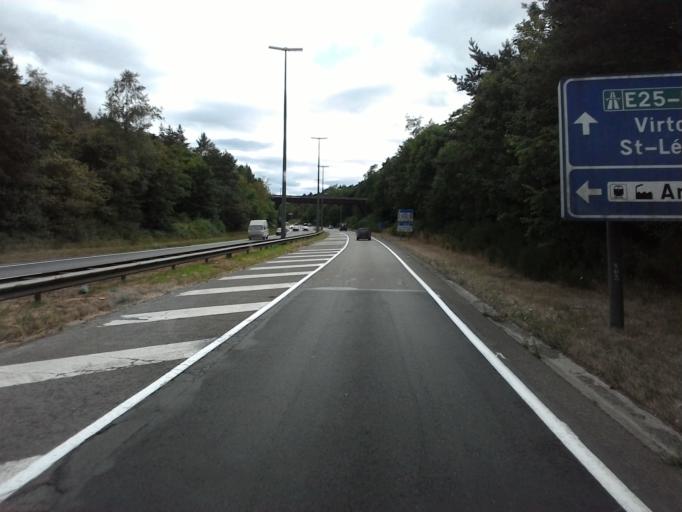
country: BE
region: Wallonia
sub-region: Province du Luxembourg
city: Arlon
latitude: 49.6797
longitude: 5.7837
